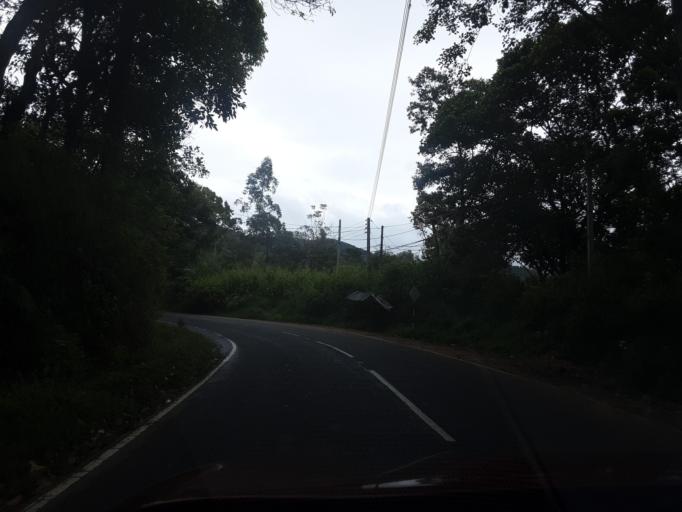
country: LK
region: Uva
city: Haputale
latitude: 6.8524
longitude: 80.9687
